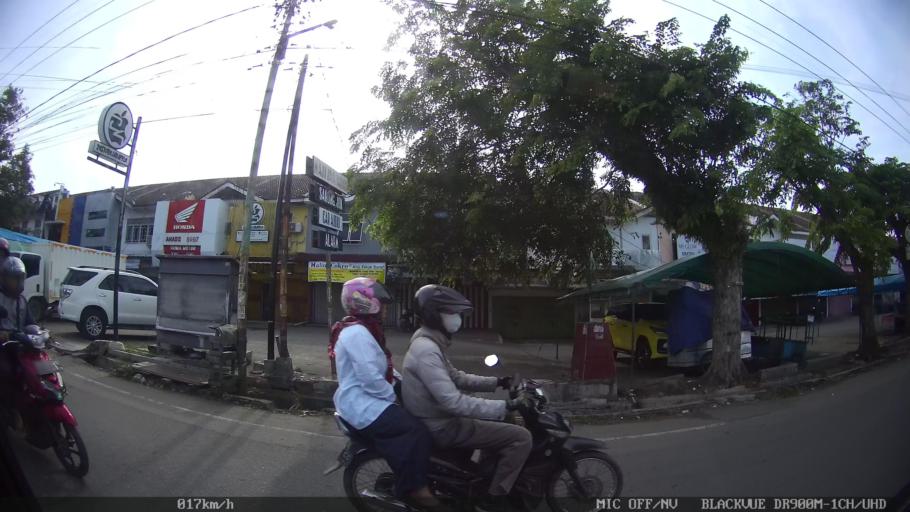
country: ID
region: Lampung
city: Kedaton
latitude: -5.3822
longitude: 105.2718
